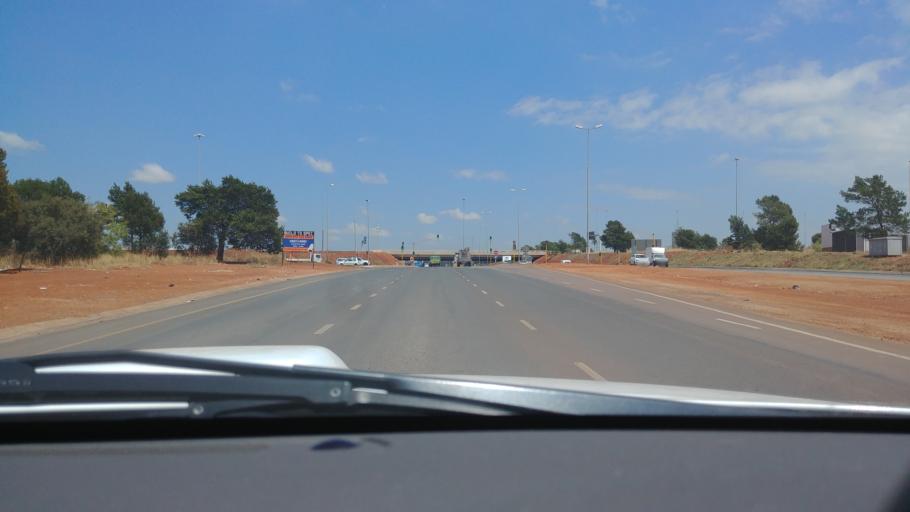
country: ZA
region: Gauteng
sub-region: Ekurhuleni Metropolitan Municipality
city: Tembisa
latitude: -26.0304
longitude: 28.2691
